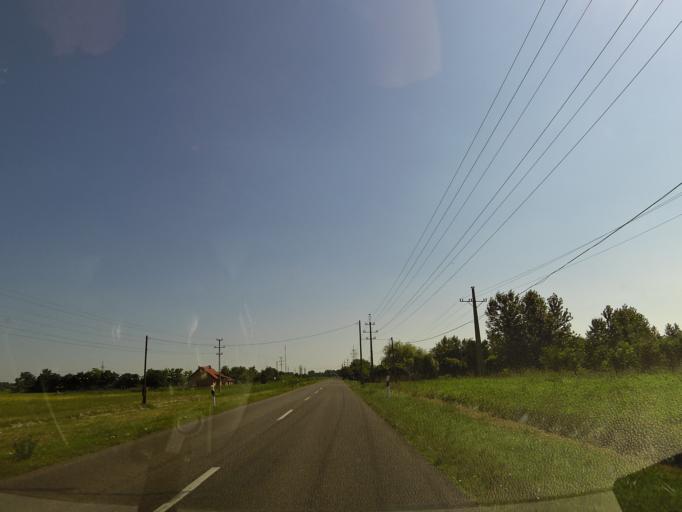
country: HU
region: Bacs-Kiskun
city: Tiszakecske
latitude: 46.9527
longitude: 20.0795
